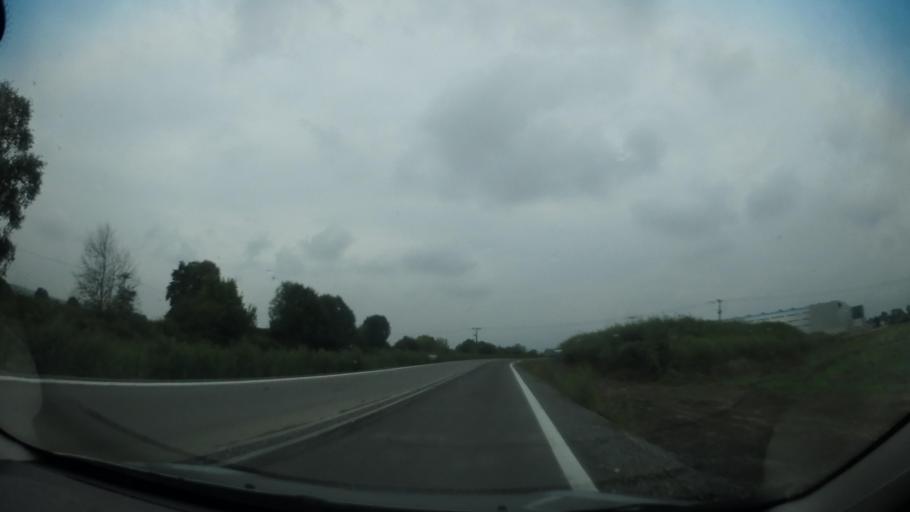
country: CZ
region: Olomoucky
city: Kojetin
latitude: 49.3370
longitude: 17.3117
